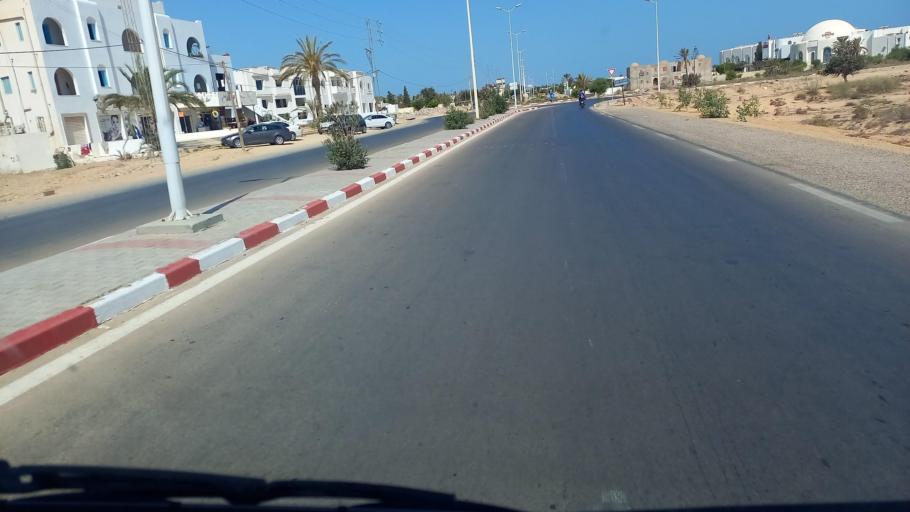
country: TN
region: Madanin
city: Midoun
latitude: 33.8555
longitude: 10.9781
